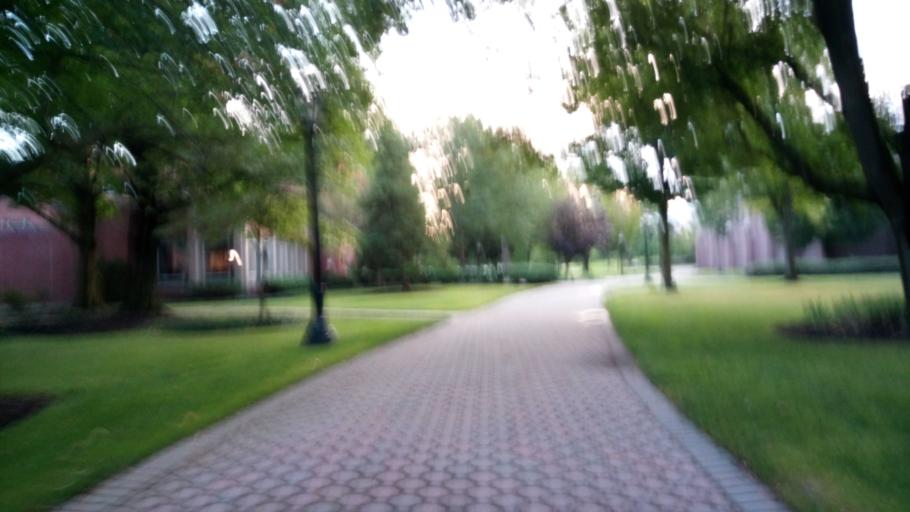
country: US
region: New York
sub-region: Chemung County
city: Elmira
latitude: 42.0964
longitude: -76.8143
